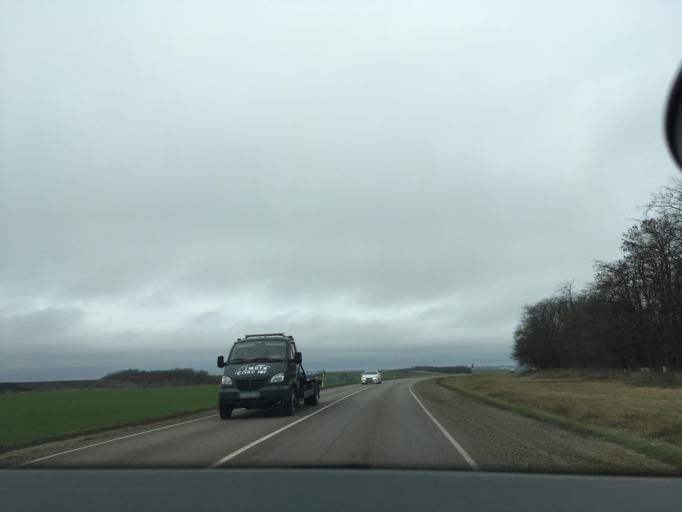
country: RU
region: Krasnodarskiy
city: Kushchevskaya
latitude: 46.6031
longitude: 39.6578
